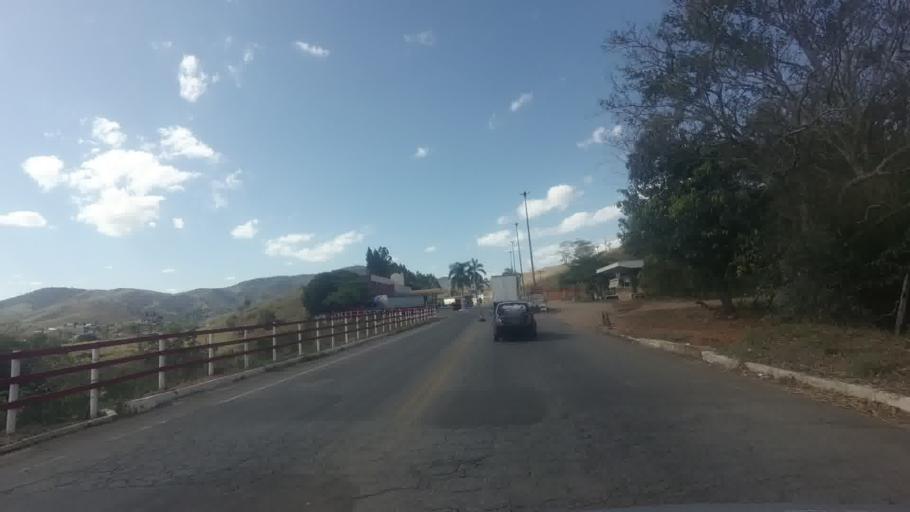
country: BR
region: Rio de Janeiro
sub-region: Bom Jesus Do Itabapoana
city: Bom Jesus do Itabapoana
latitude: -21.1338
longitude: -41.6608
